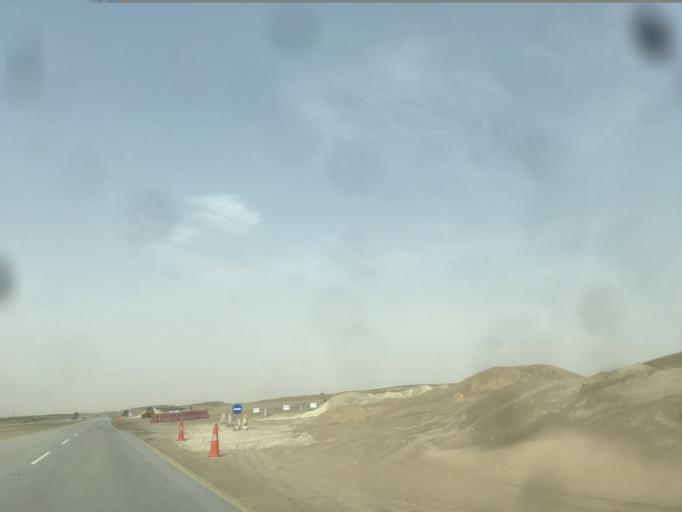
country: SA
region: Eastern Province
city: Abqaiq
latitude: 25.9086
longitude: 49.8874
